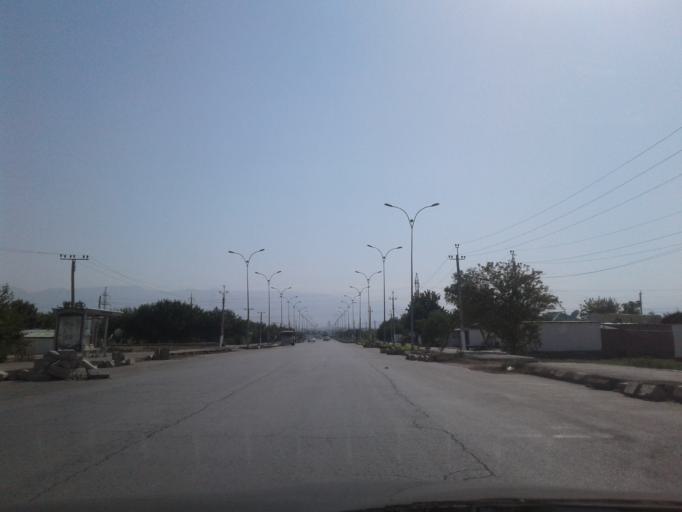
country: TM
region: Ahal
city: Ashgabat
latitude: 37.9732
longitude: 58.4298
